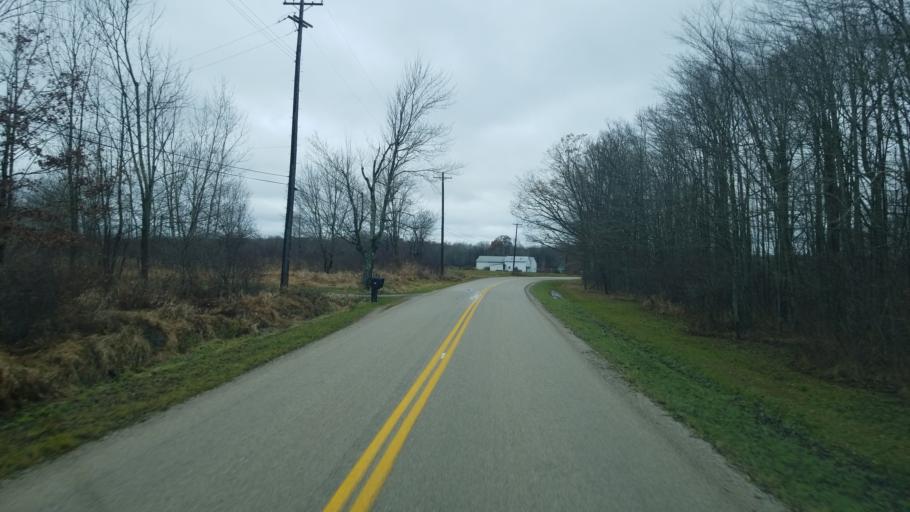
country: US
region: Ohio
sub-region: Ashtabula County
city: Andover
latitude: 41.7197
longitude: -80.6249
